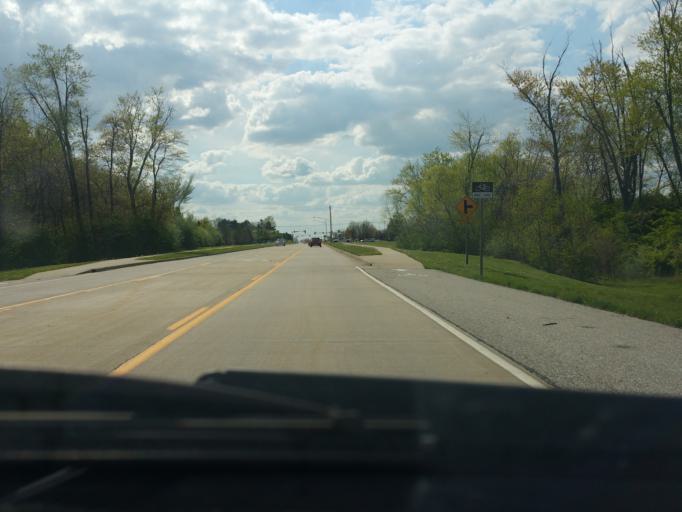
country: US
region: Illinois
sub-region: Madison County
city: Edwardsville
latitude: 38.7873
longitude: -89.9455
